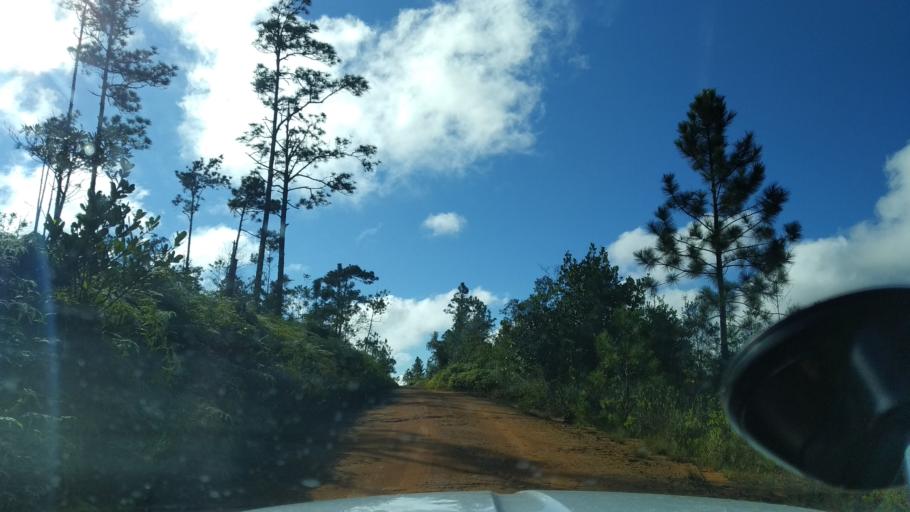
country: BZ
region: Cayo
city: Belmopan
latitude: 16.9991
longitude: -88.8492
